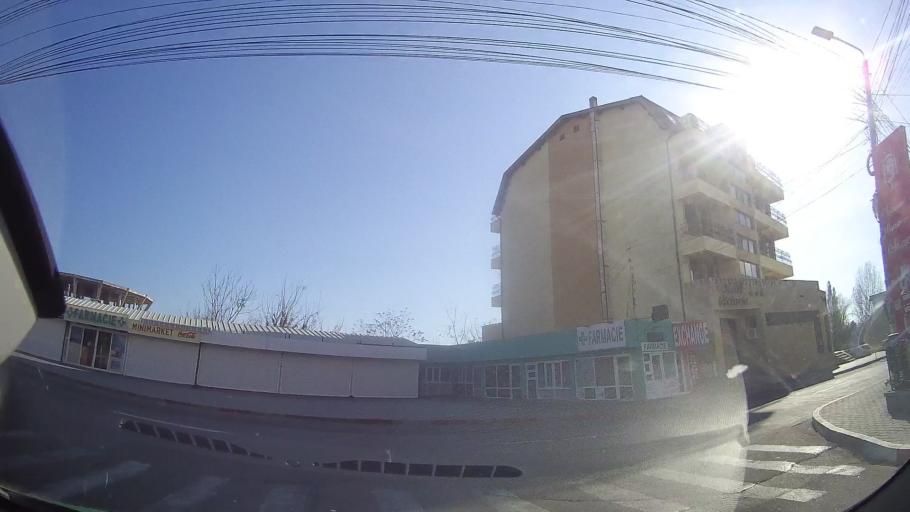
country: RO
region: Constanta
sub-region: Comuna Costinesti
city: Costinesti
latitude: 43.9488
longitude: 28.6338
